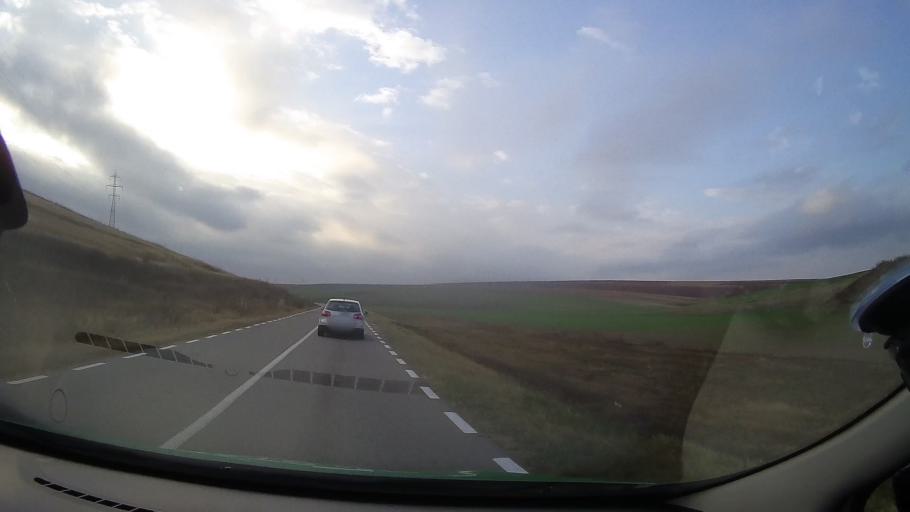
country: RO
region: Constanta
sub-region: Comuna Pestera
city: Pestera
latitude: 44.2032
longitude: 28.1486
